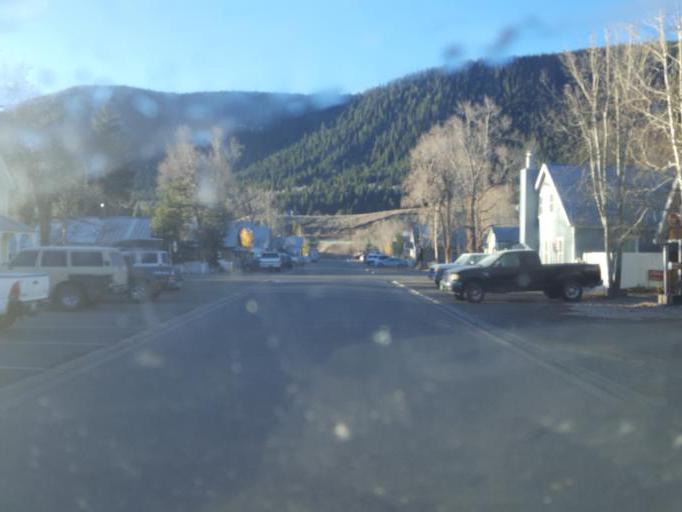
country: US
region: Colorado
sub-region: Gunnison County
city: Crested Butte
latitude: 38.8694
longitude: -106.9858
